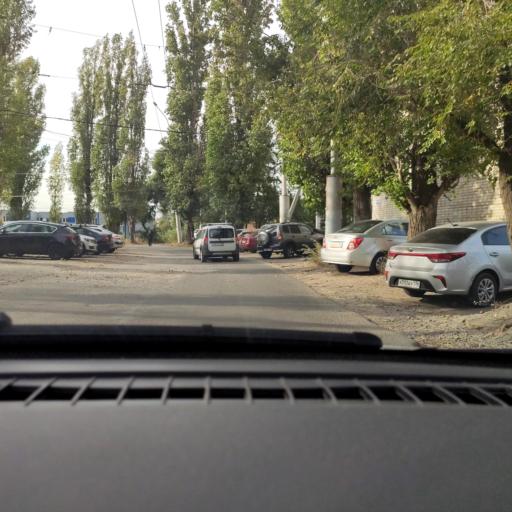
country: RU
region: Voronezj
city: Voronezh
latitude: 51.7012
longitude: 39.2738
